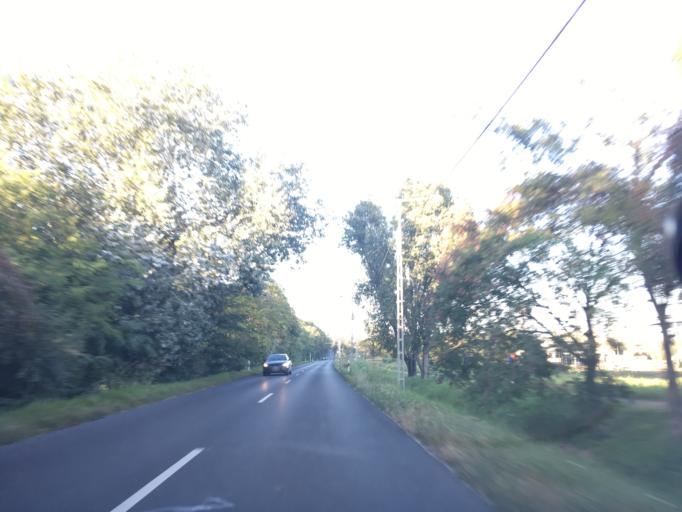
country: HU
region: Pest
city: Szazhalombatta
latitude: 47.3067
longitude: 18.8960
